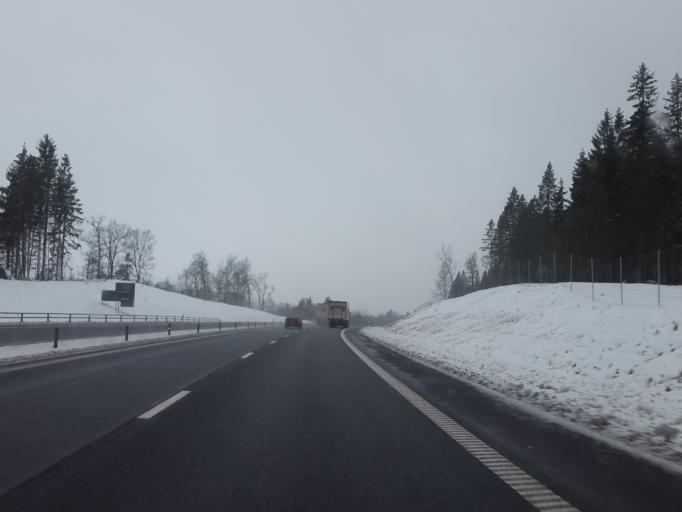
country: SE
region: Vaestra Goetaland
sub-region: Ulricehamns Kommun
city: Ulricehamn
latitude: 57.8150
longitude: 13.2650
